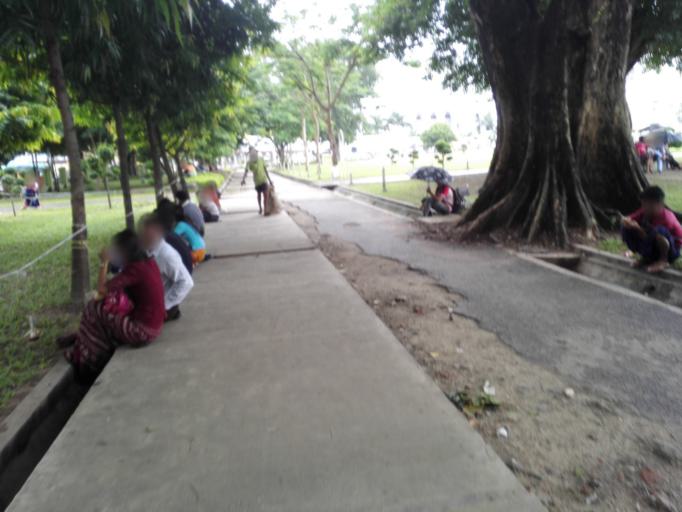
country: MM
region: Yangon
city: Yangon
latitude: 16.7729
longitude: 96.1590
